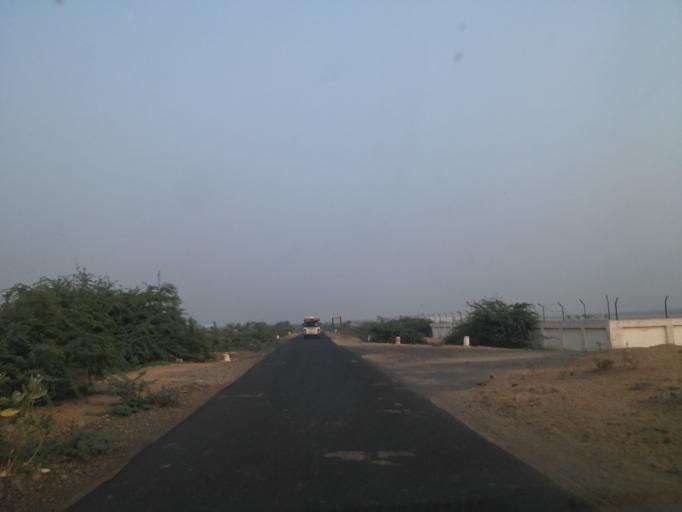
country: IN
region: Gujarat
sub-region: Kachchh
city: Mandvi
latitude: 22.8422
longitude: 69.3038
